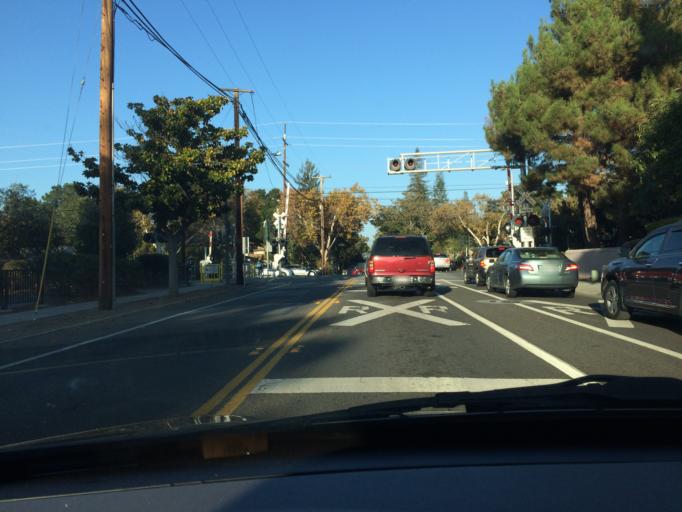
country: US
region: California
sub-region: Santa Clara County
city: Palo Alto
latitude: 37.4352
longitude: -122.1520
